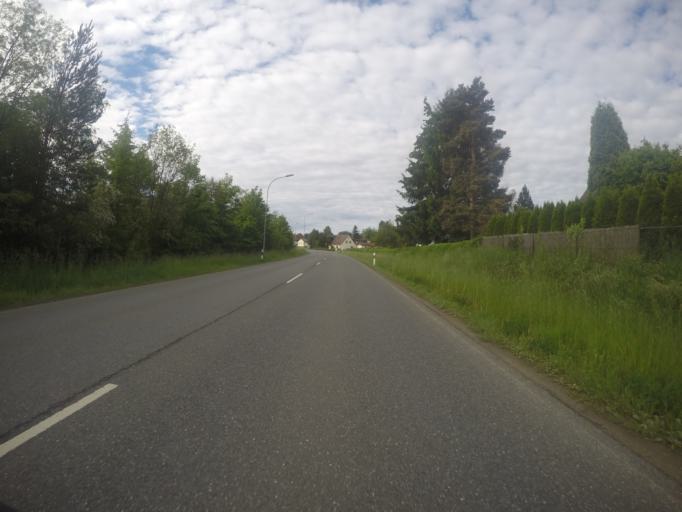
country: DE
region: Bavaria
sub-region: Upper Franconia
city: Schonwald
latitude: 50.2073
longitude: 12.0945
